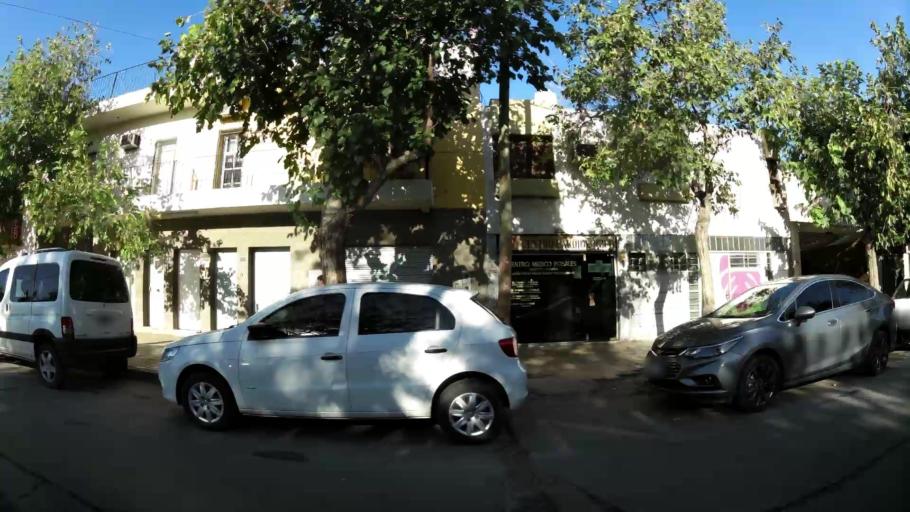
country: AR
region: San Juan
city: San Juan
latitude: -31.5394
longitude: -68.5212
